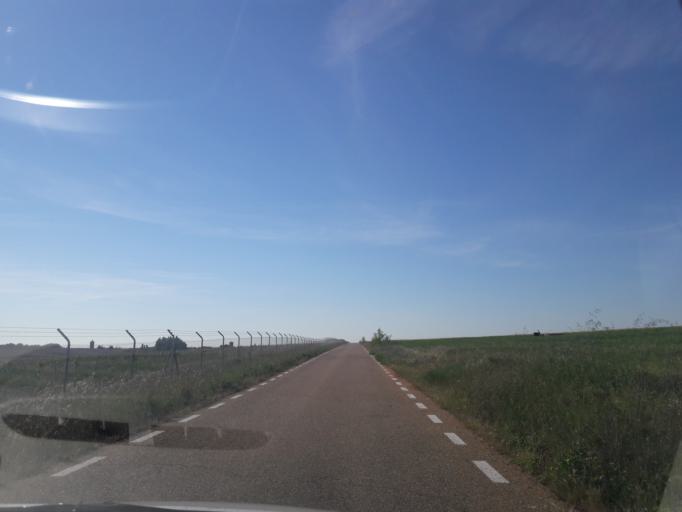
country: ES
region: Castille and Leon
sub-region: Provincia de Salamanca
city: Parada de Rubiales
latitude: 41.1548
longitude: -5.4477
